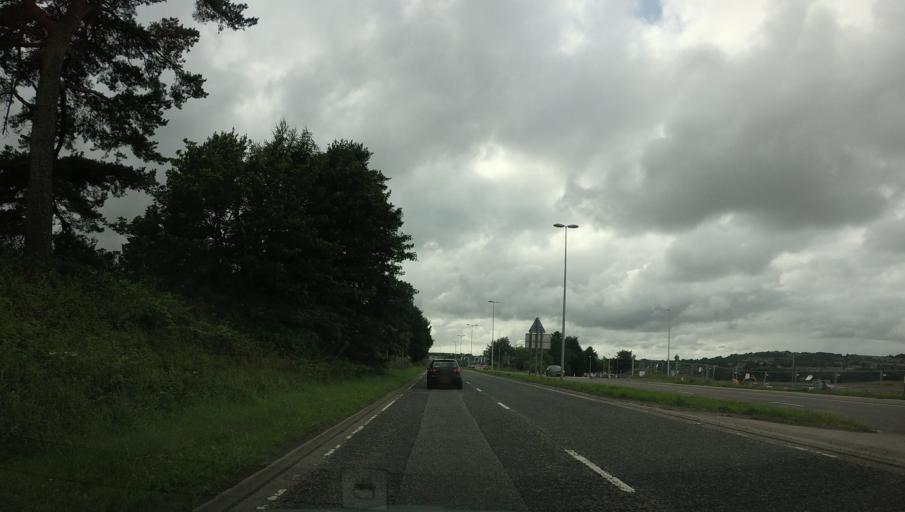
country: GB
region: Scotland
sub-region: Aberdeenshire
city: Westhill
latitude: 57.1472
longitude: -2.2576
